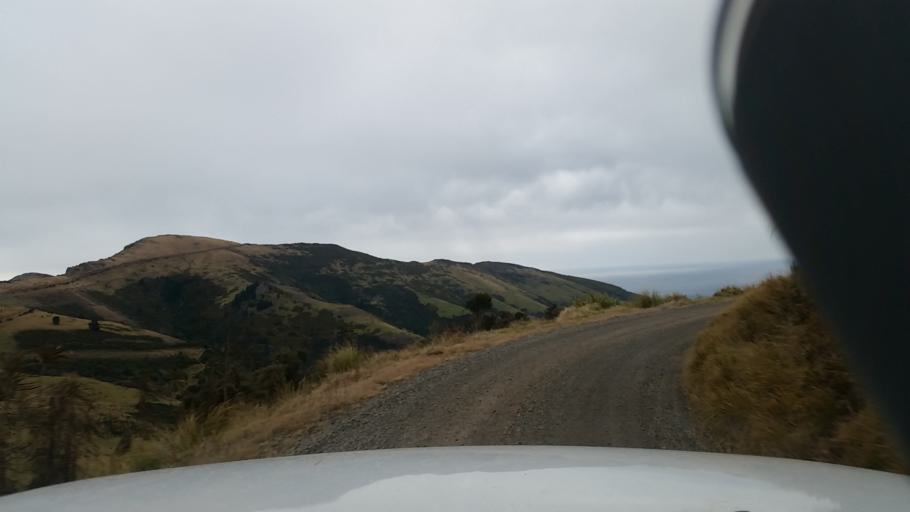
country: NZ
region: Canterbury
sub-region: Christchurch City
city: Christchurch
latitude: -43.8092
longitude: 172.8560
